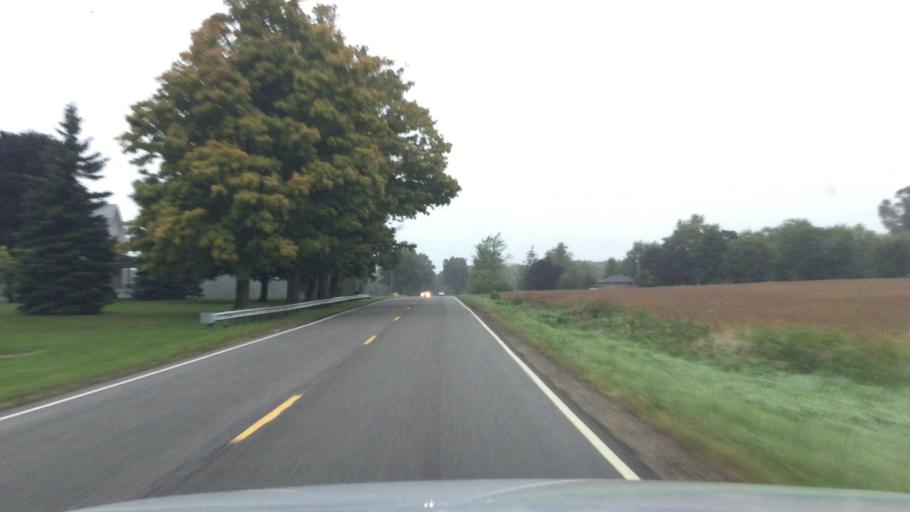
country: US
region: Michigan
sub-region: Shiawassee County
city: Corunna
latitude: 42.9257
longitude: -84.1242
